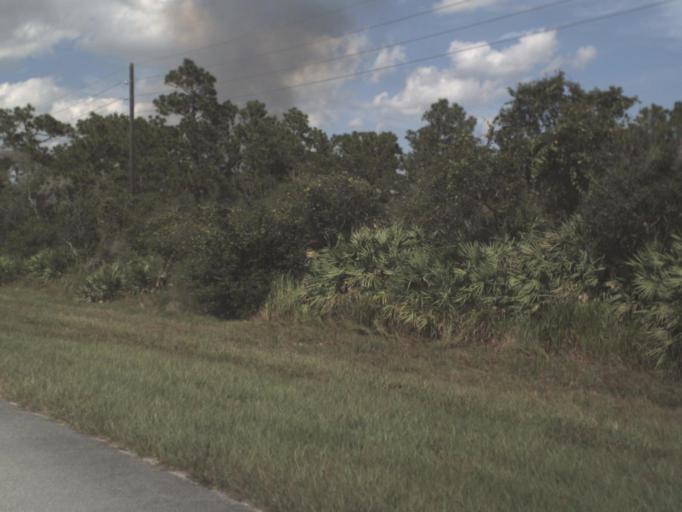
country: US
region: Florida
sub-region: Okeechobee County
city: Cypress Quarters
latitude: 27.5407
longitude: -80.8125
